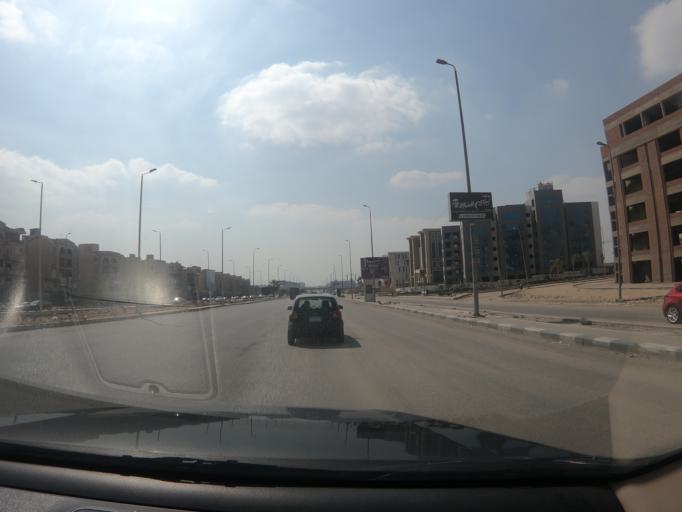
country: EG
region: Muhafazat al Qalyubiyah
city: Al Khankah
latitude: 30.0256
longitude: 31.4802
